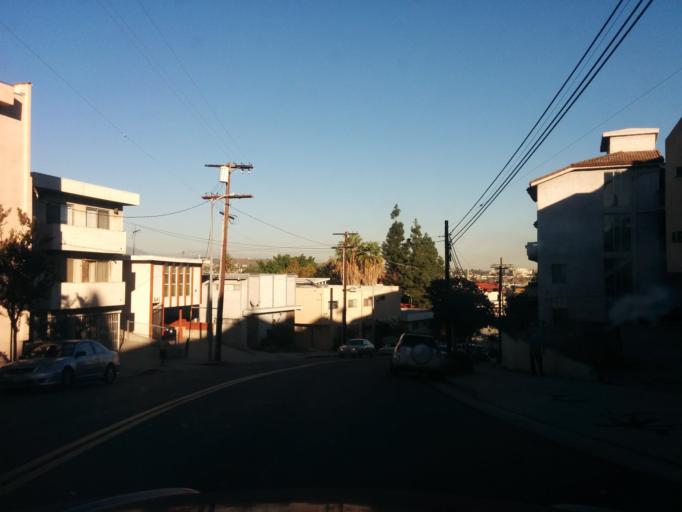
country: US
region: California
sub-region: Los Angeles County
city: Los Angeles
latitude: 34.0635
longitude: -118.2427
